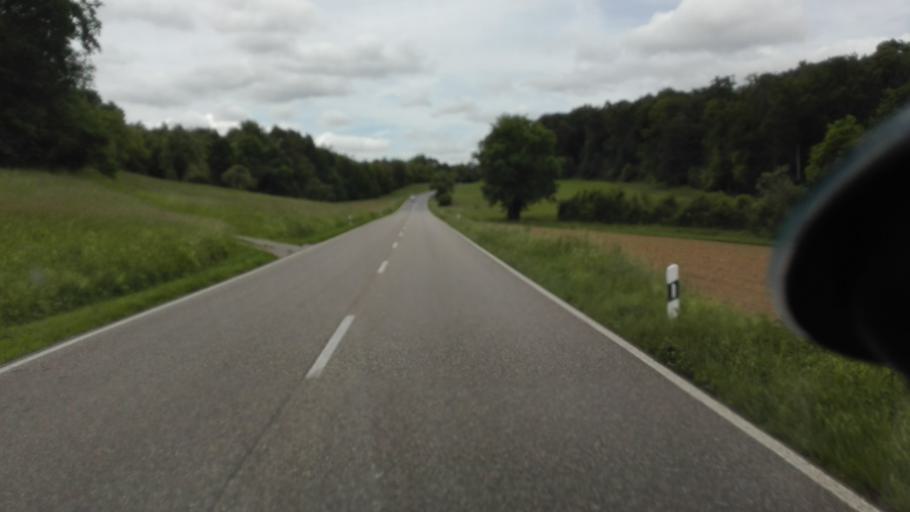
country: DE
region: Baden-Wuerttemberg
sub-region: Karlsruhe Region
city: Gondelsheim
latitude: 49.0293
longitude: 8.6574
